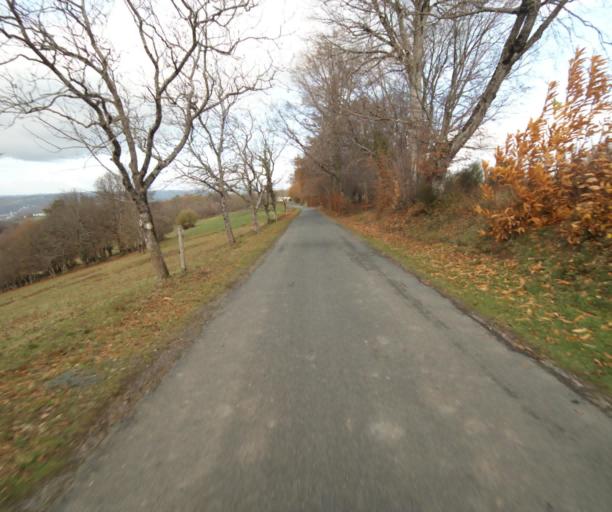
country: FR
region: Limousin
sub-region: Departement de la Correze
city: Laguenne
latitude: 45.2231
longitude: 1.7919
